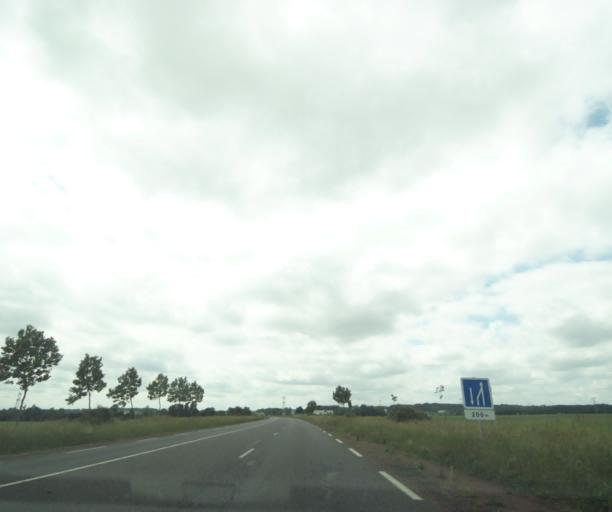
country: FR
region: Poitou-Charentes
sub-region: Departement des Deux-Sevres
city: Saint-Varent
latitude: 46.8390
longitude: -0.2083
